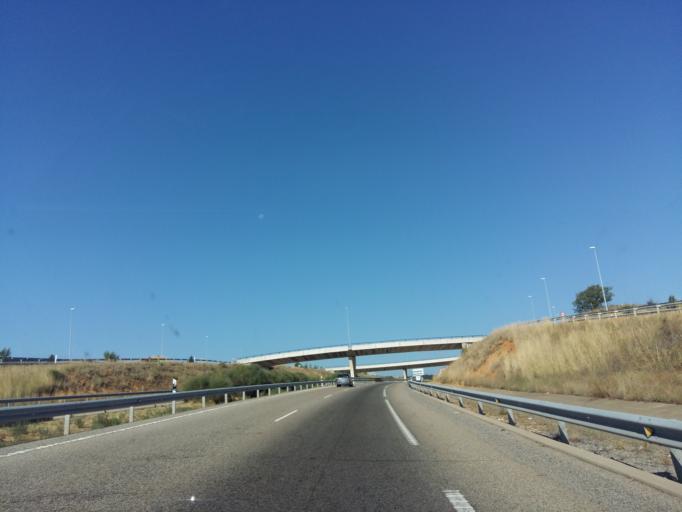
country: ES
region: Castille and Leon
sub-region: Provincia de Leon
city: Leon
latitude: 42.5671
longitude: -5.5935
